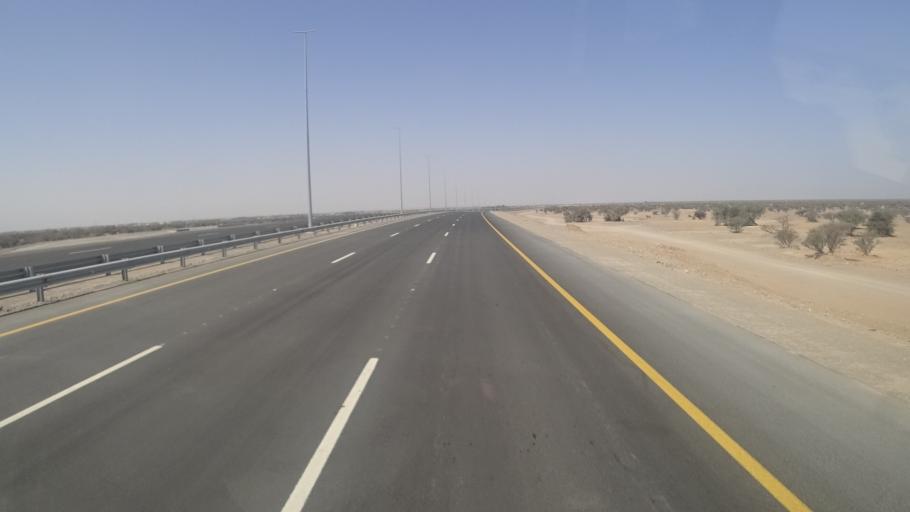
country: OM
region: Ash Sharqiyah
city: Sur
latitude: 22.2722
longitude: 59.2483
